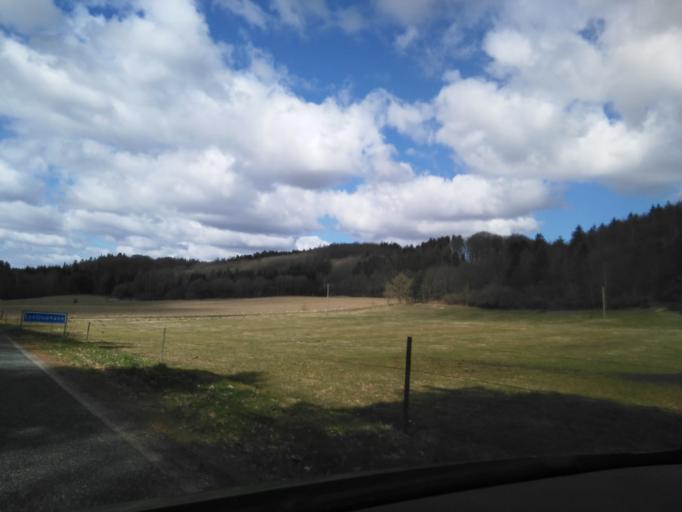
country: DK
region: Central Jutland
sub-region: Silkeborg Kommune
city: Virklund
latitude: 56.0319
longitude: 9.4944
